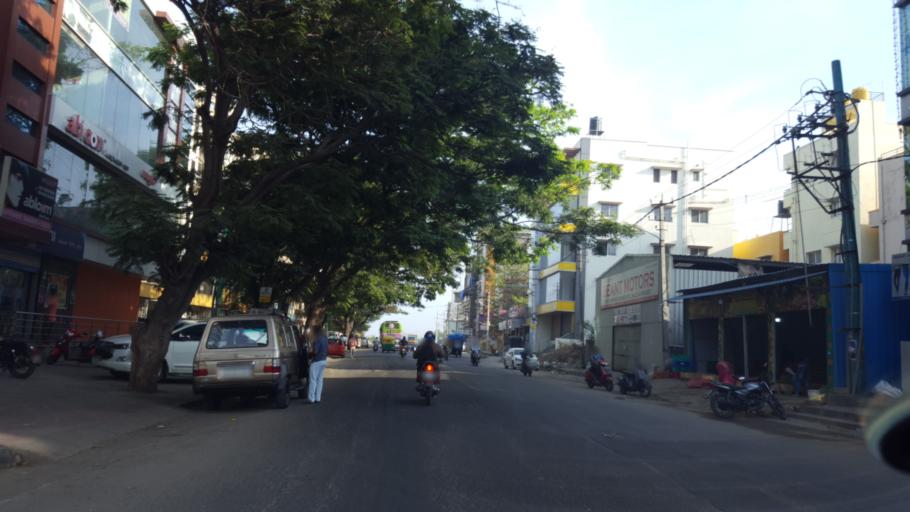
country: IN
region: Karnataka
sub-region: Bangalore Urban
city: Bangalore
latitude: 12.9161
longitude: 77.5134
